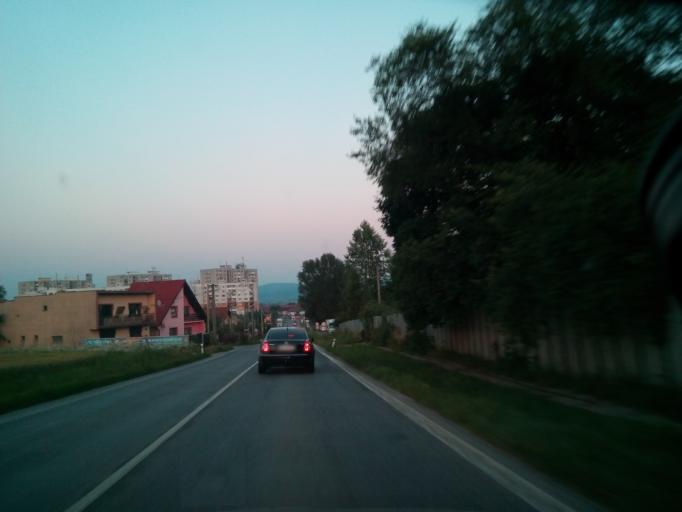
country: SK
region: Kosicky
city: Spisska Nova Ves
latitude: 48.9587
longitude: 20.5095
